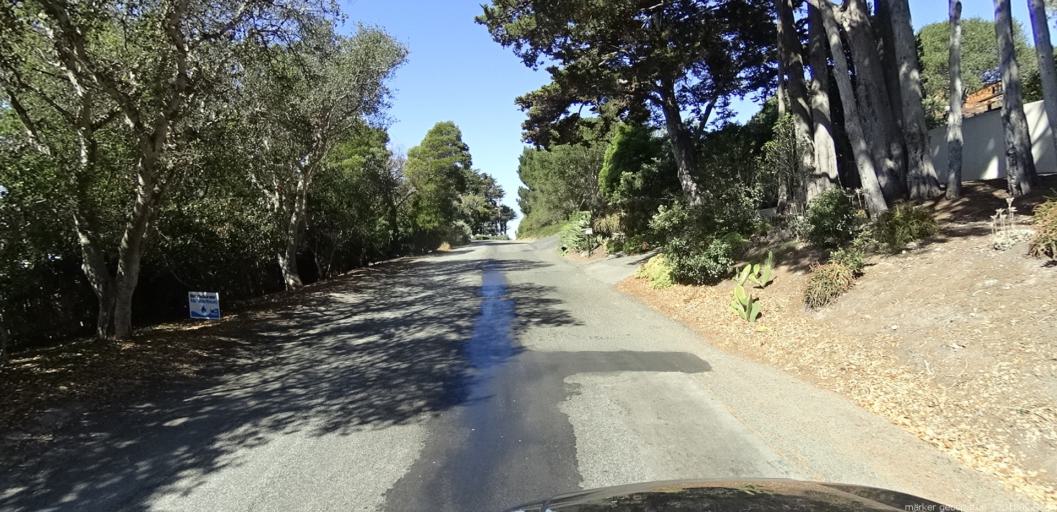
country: US
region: California
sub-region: Monterey County
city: Carmel-by-the-Sea
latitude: 36.5477
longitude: -121.9119
